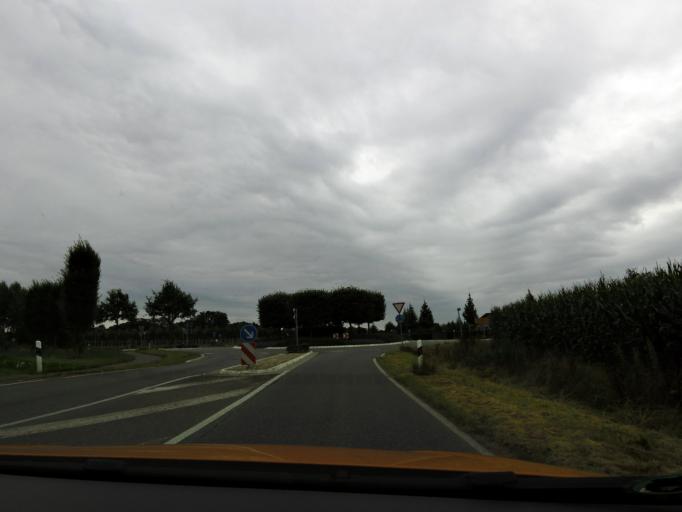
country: DE
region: Lower Saxony
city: Bad Zwischenahn
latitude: 53.2333
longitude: 7.9915
